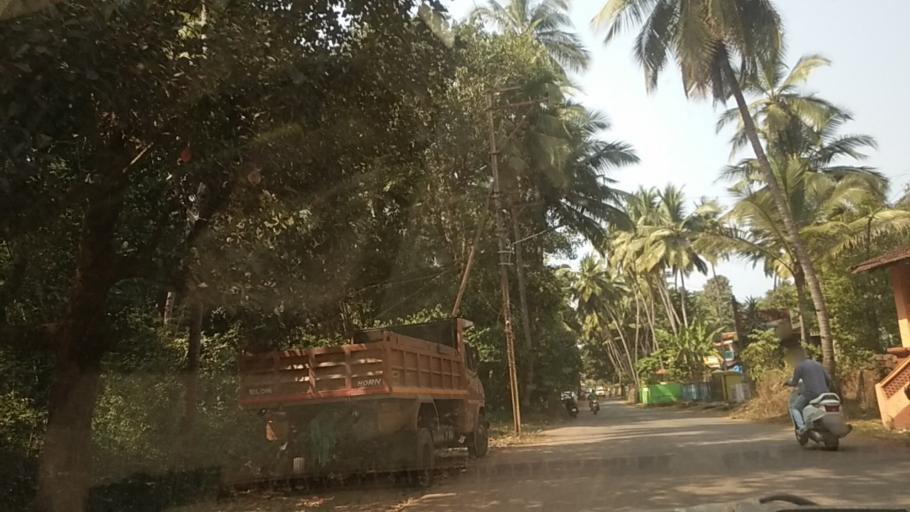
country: IN
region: Goa
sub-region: South Goa
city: Cavelossim
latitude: 15.1391
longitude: 73.9572
